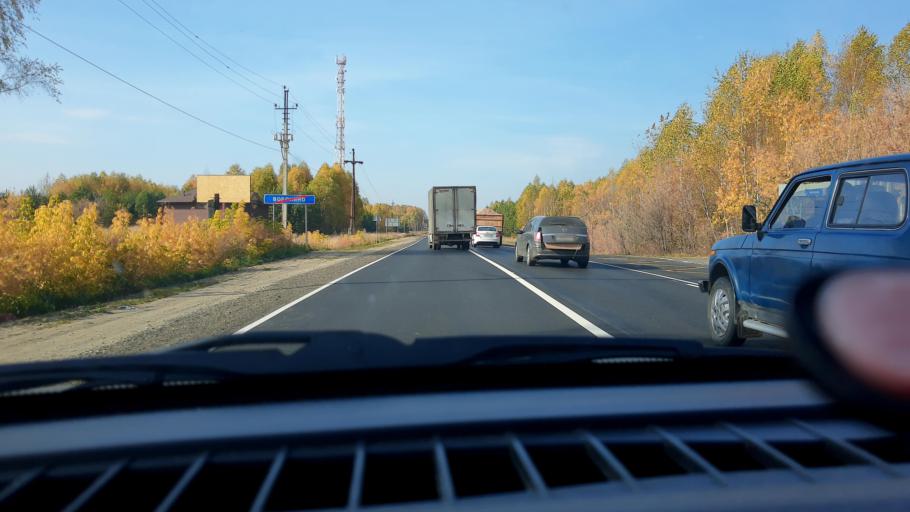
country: RU
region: Nizjnij Novgorod
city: Novaya Balakhna
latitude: 56.5983
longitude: 43.6396
